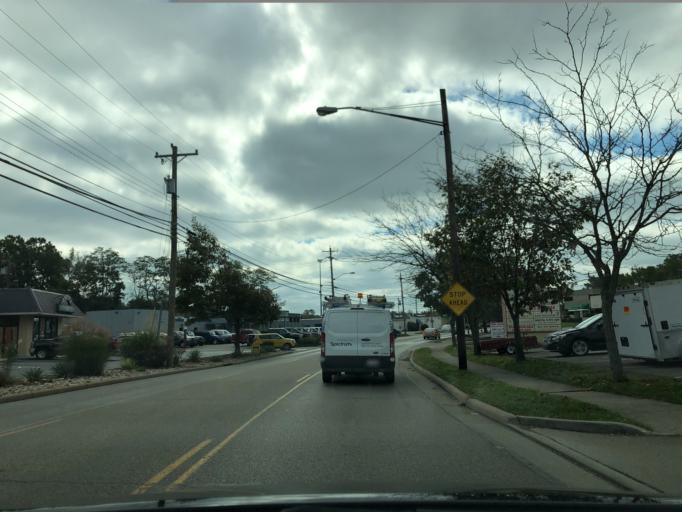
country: US
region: Ohio
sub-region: Hamilton County
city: Loveland
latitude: 39.2665
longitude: -84.2662
